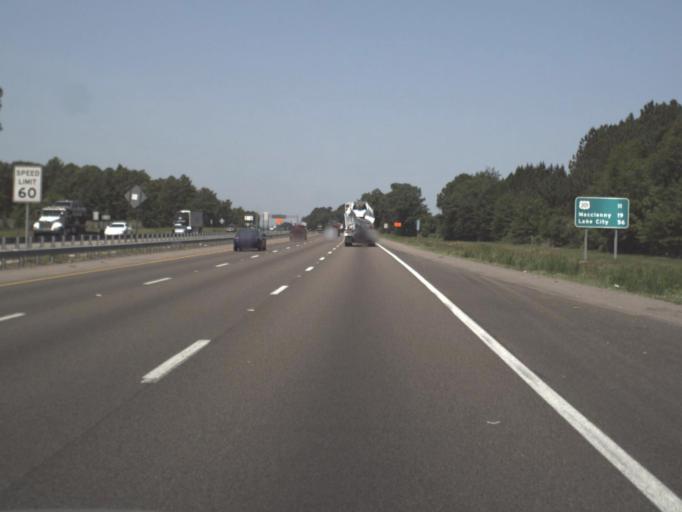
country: US
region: Florida
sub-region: Duval County
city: Jacksonville
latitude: 30.3148
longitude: -81.7990
